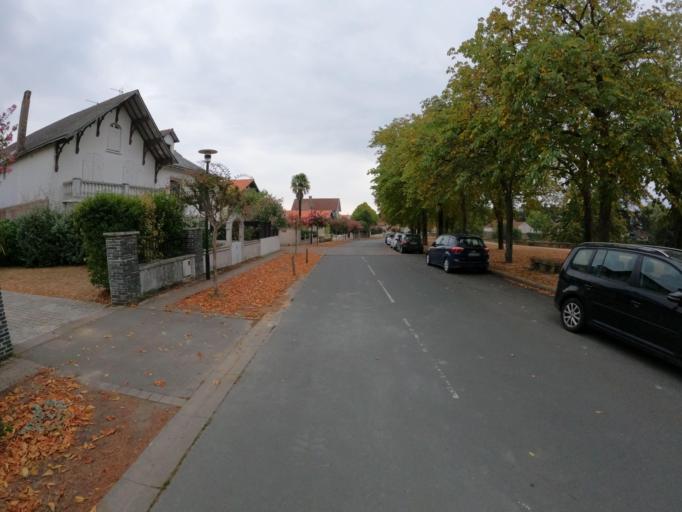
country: FR
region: Pays de la Loire
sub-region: Departement de la Vendee
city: Montaigu
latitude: 46.9773
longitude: -1.3092
